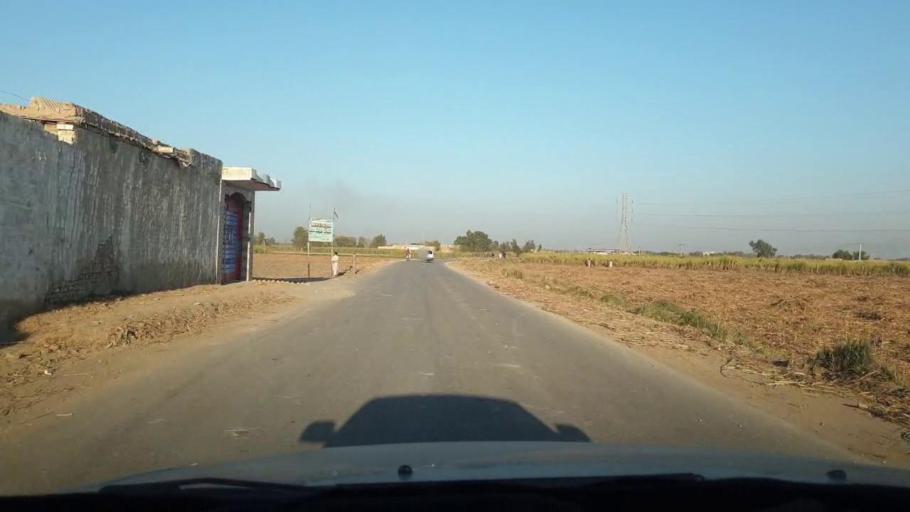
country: PK
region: Sindh
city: Ghotki
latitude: 27.9967
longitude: 69.2781
